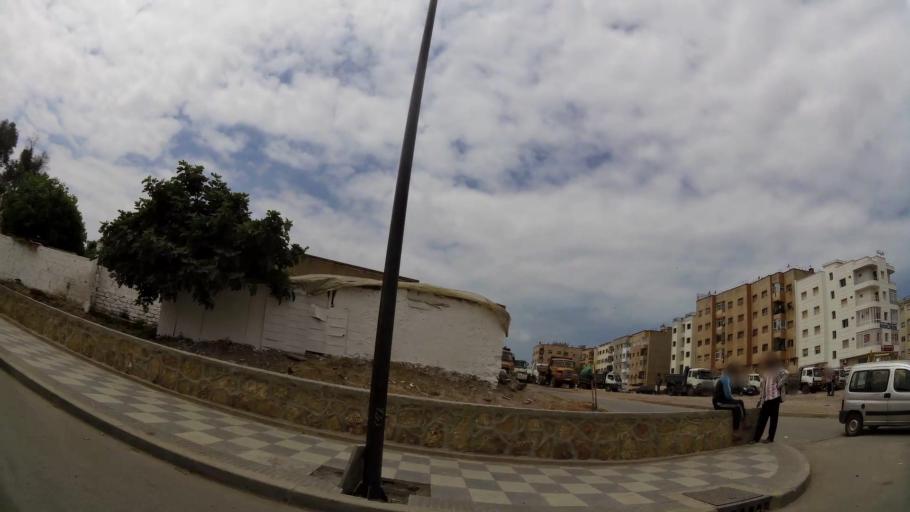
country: MA
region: Rabat-Sale-Zemmour-Zaer
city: Sale
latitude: 34.0609
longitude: -6.7824
